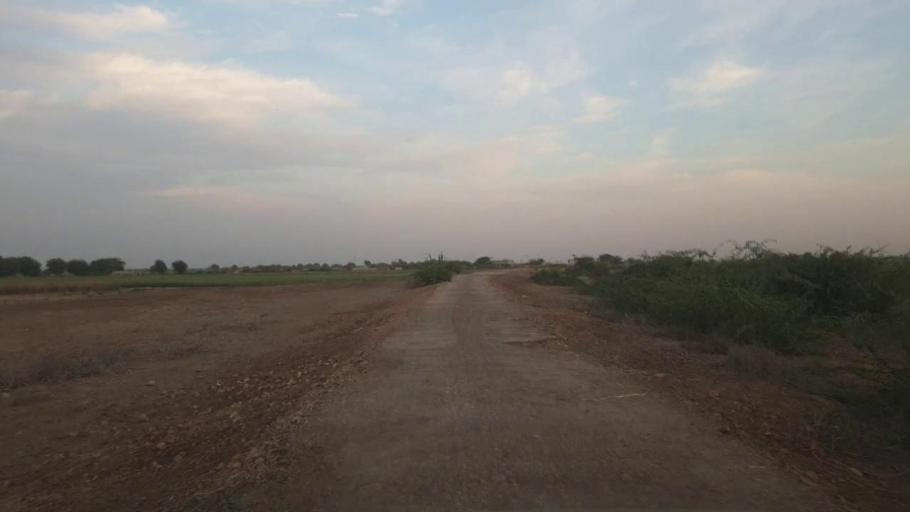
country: PK
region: Sindh
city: Umarkot
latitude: 25.2669
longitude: 69.6674
